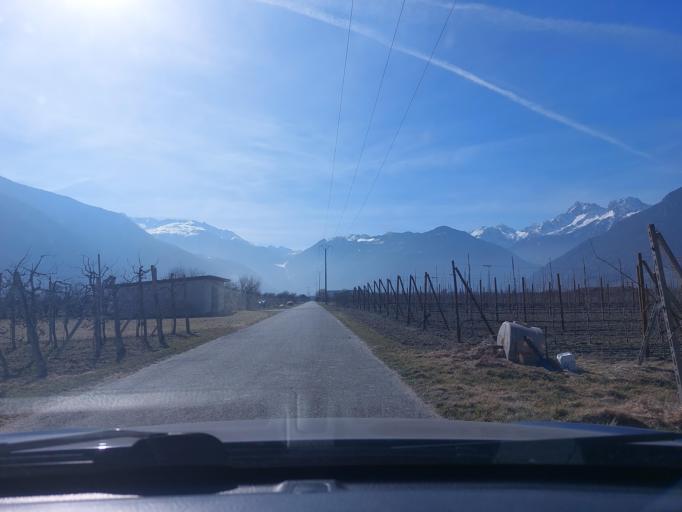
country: CH
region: Valais
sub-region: Martigny District
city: Charrat-les-Chenes
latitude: 46.1327
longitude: 7.1430
